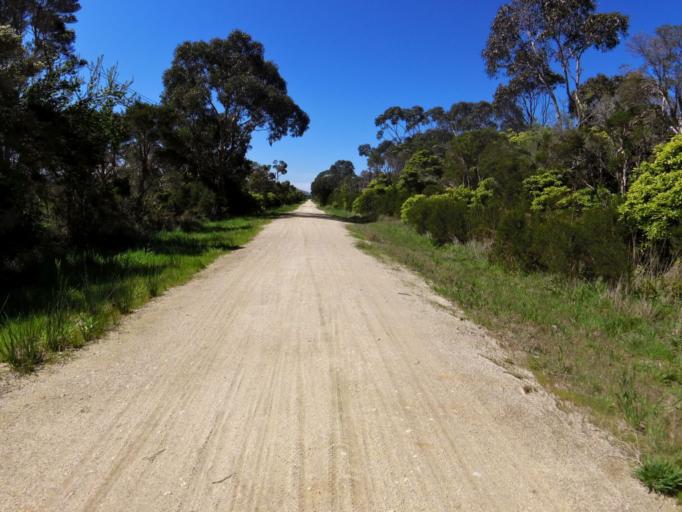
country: AU
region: Victoria
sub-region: Latrobe
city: Morwell
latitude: -38.6664
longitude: 146.2891
